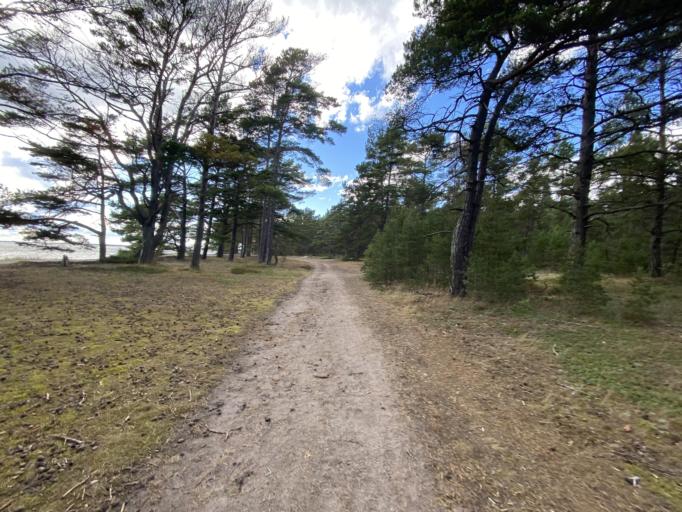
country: SE
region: Stockholm
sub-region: Varmdo Kommun
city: Holo
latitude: 59.2786
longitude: 18.9093
